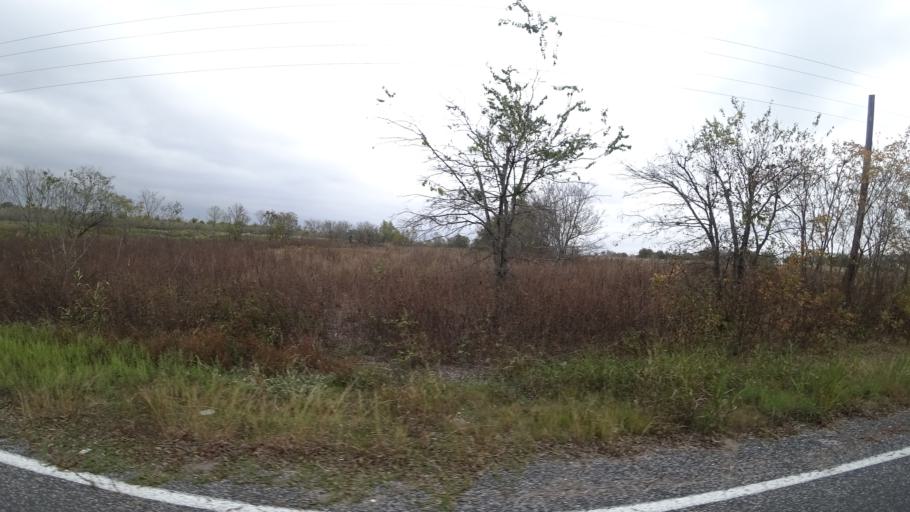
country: US
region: Texas
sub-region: Travis County
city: Pflugerville
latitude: 30.3931
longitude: -97.5862
